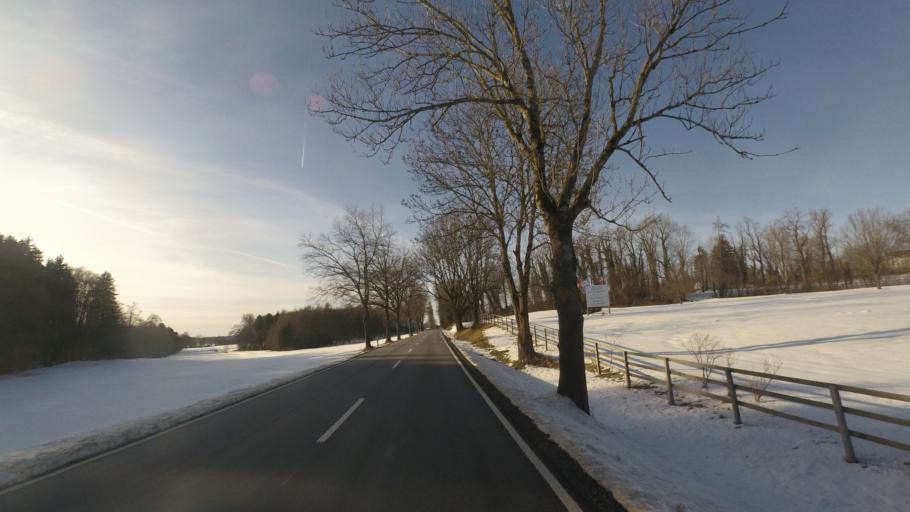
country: DE
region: Bavaria
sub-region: Upper Bavaria
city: Chieming
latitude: 47.9200
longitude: 12.5062
